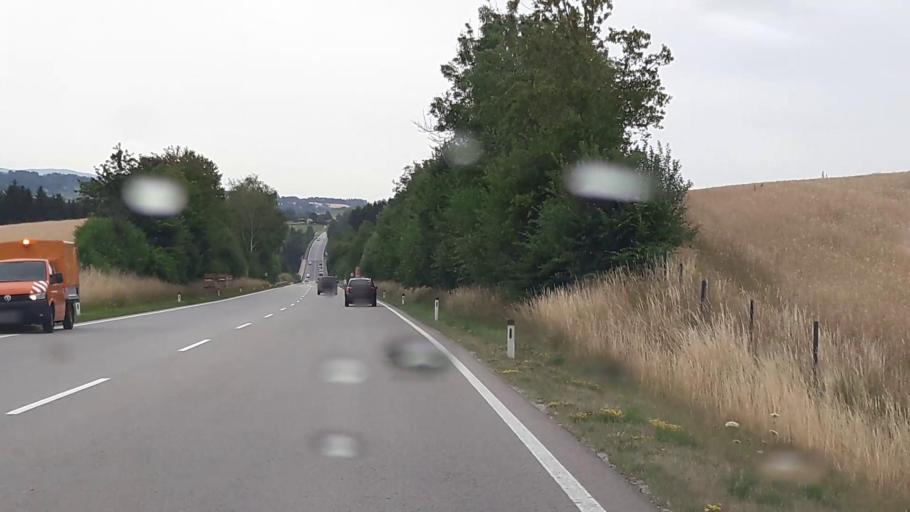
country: AT
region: Upper Austria
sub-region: Politischer Bezirk Rohrbach
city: Kleinzell im Muehlkreis
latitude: 48.4821
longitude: 13.9850
